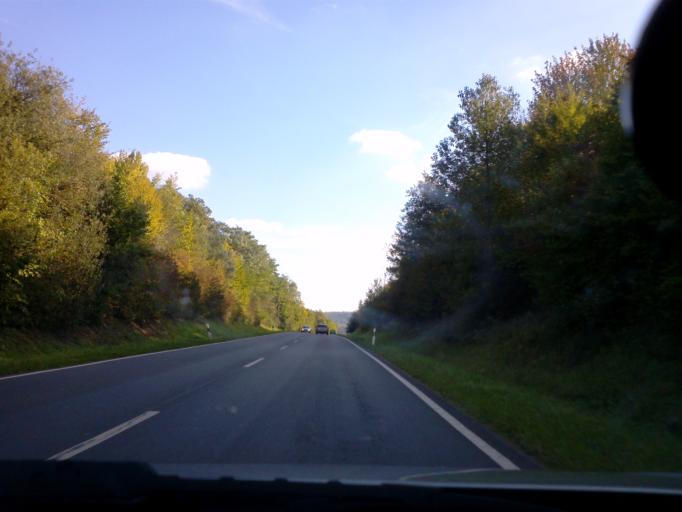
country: DE
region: Baden-Wuerttemberg
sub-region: Regierungsbezirk Stuttgart
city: Gemmingen
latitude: 49.1403
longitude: 8.9957
